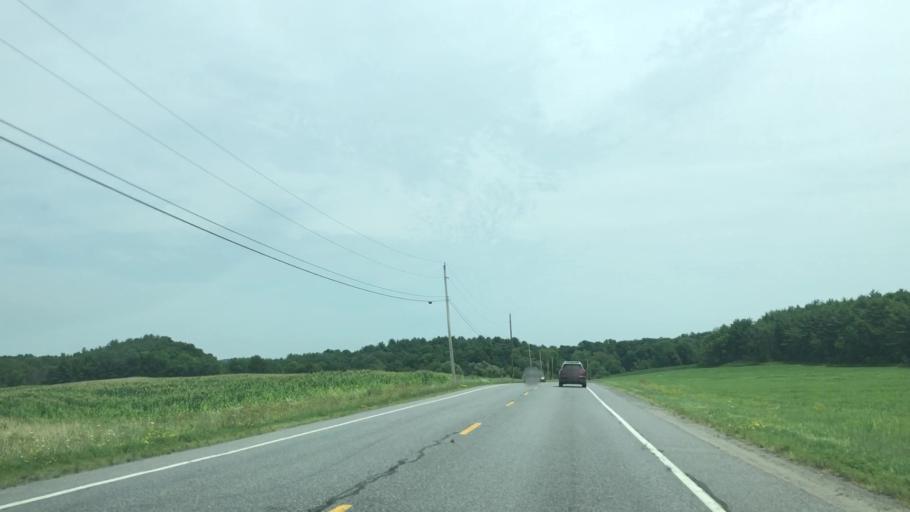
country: US
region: New York
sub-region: Warren County
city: Queensbury
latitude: 43.4059
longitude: -73.5307
